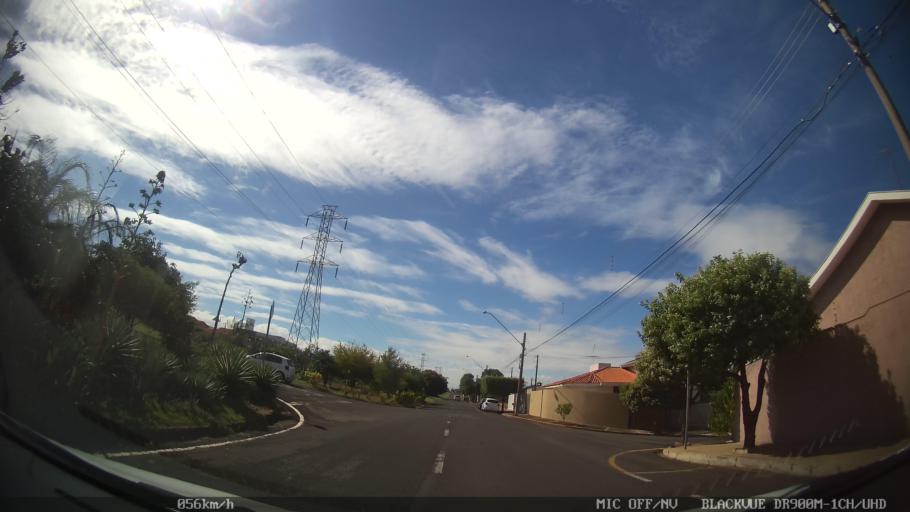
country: BR
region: Sao Paulo
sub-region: Sao Jose Do Rio Preto
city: Sao Jose do Rio Preto
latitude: -20.8404
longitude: -49.3588
